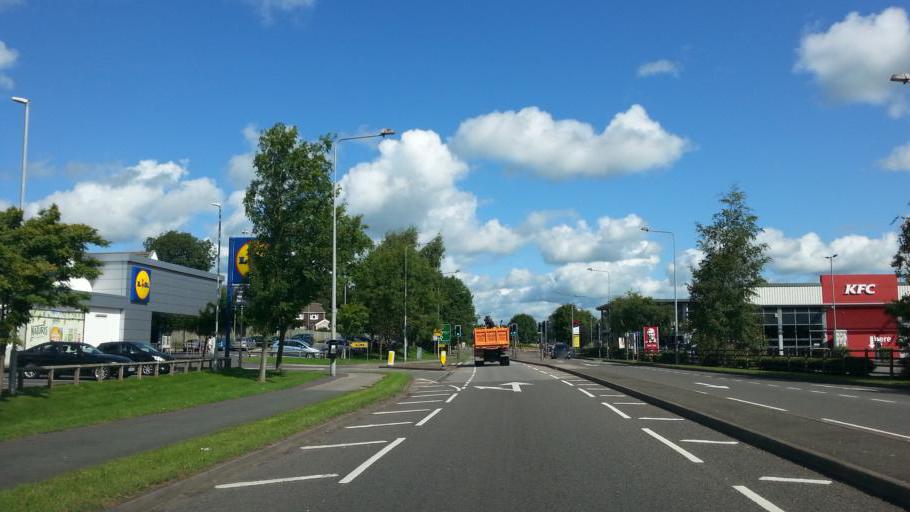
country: GB
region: England
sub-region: Staffordshire
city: Uttoxeter
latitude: 52.8995
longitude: -1.8603
